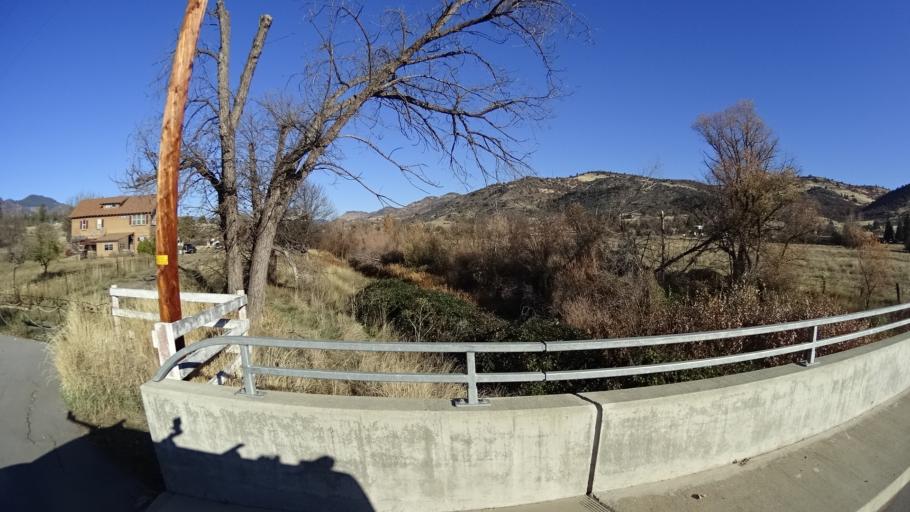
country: US
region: California
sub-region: Siskiyou County
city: Montague
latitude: 41.9121
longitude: -122.5599
